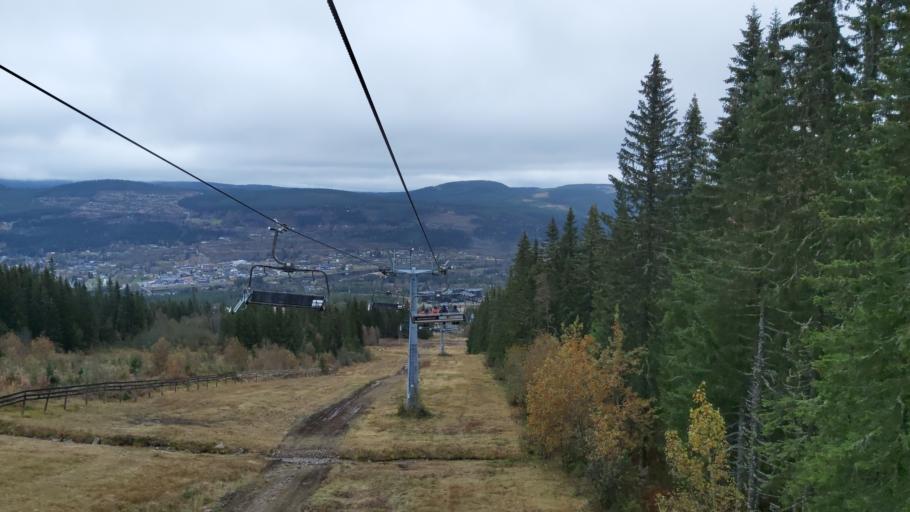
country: NO
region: Hedmark
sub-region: Trysil
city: Innbygda
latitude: 61.3083
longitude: 12.2212
